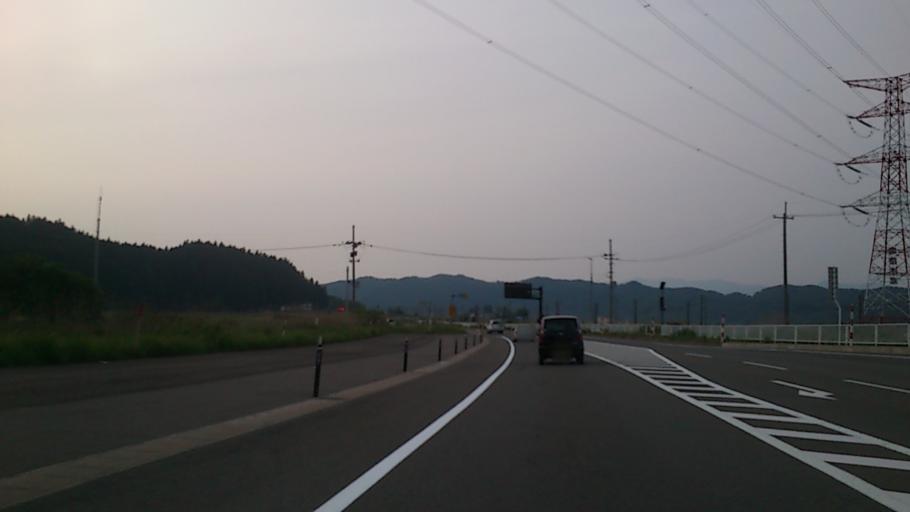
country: JP
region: Akita
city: Noshiromachi
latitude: 40.2120
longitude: 140.1989
